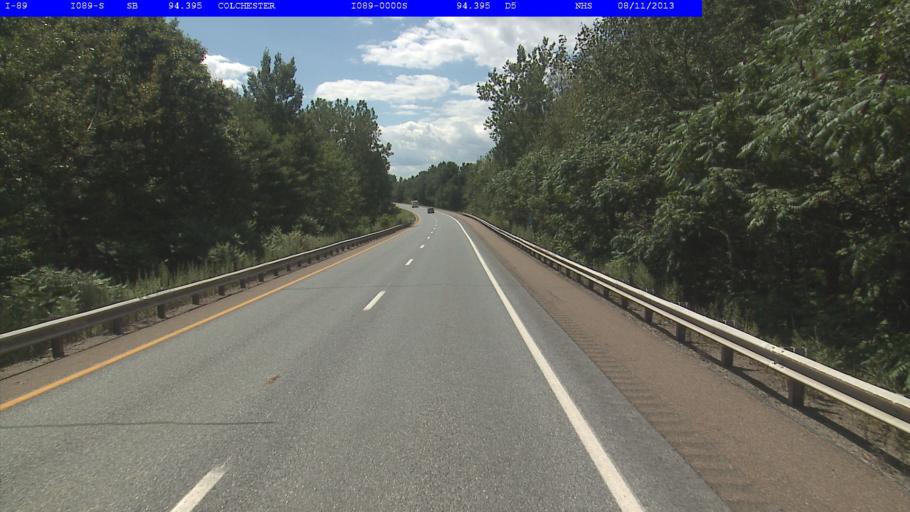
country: US
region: Vermont
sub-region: Chittenden County
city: Colchester
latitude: 44.5436
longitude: -73.1961
